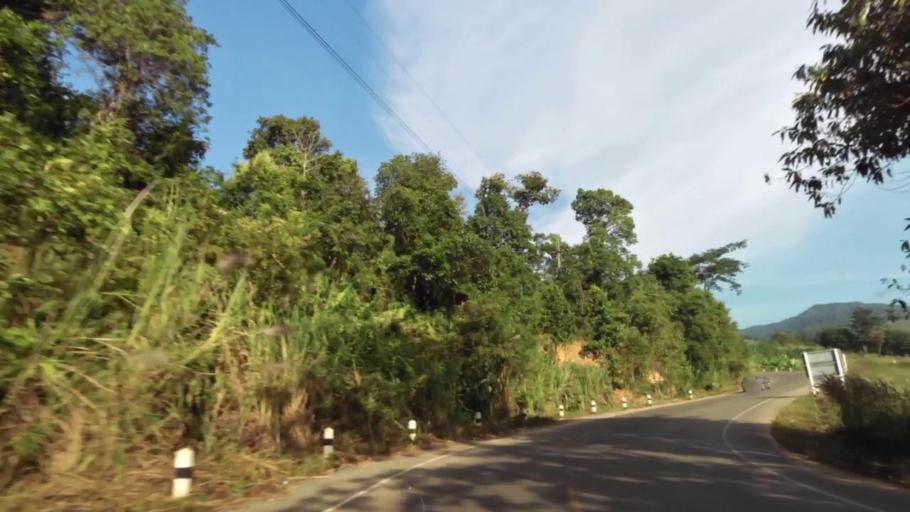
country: TH
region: Chiang Rai
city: Khun Tan
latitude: 19.8673
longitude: 100.4080
